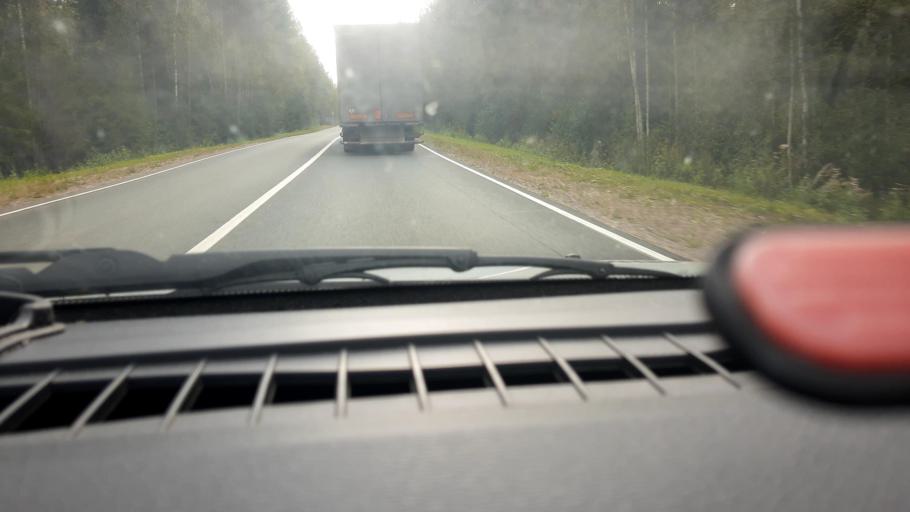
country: RU
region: Nizjnij Novgorod
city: Uren'
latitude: 57.2913
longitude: 45.6499
